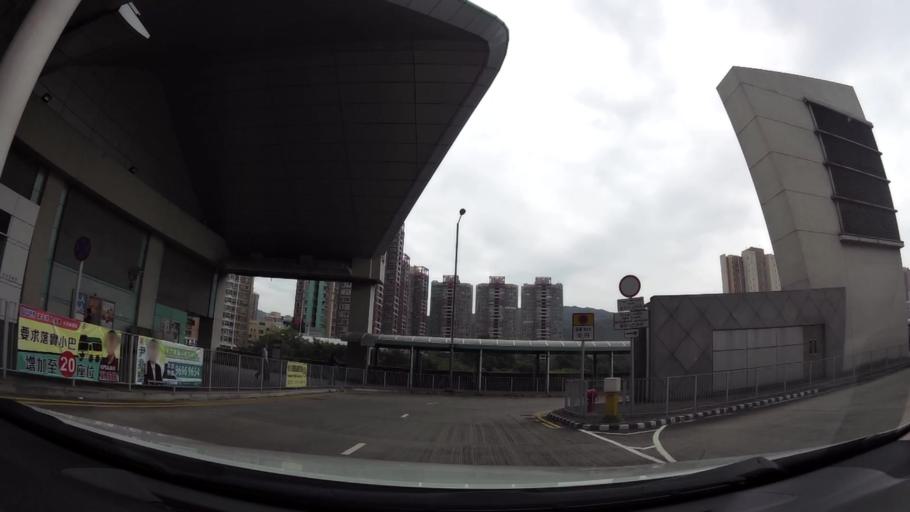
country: HK
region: Tuen Mun
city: Tuen Mun
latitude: 22.4108
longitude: 113.9785
